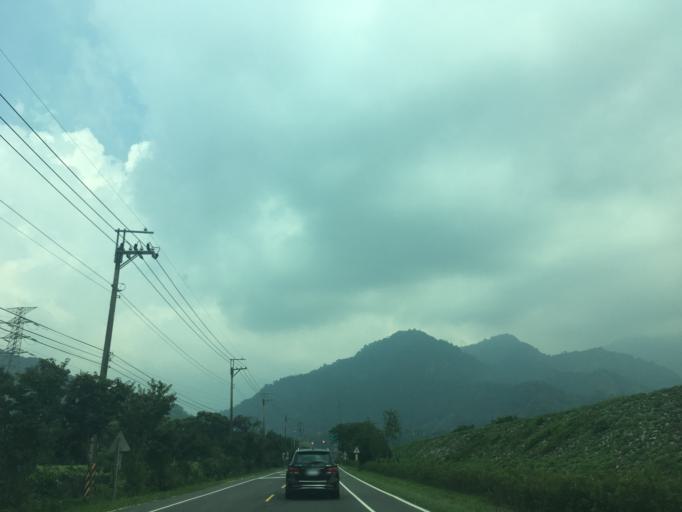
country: TW
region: Taiwan
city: Fengyuan
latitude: 24.2959
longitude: 120.8939
